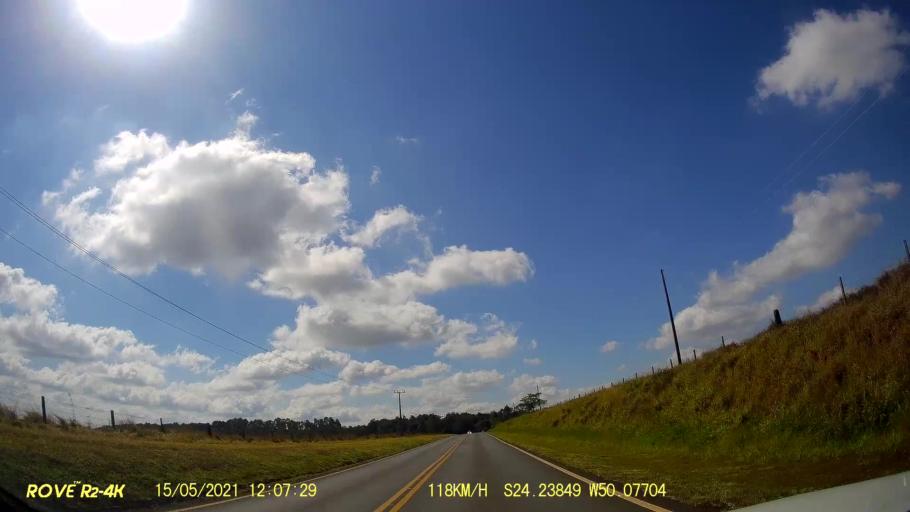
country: BR
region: Parana
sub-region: Pirai Do Sul
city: Pirai do Sul
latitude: -24.2386
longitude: -50.0773
